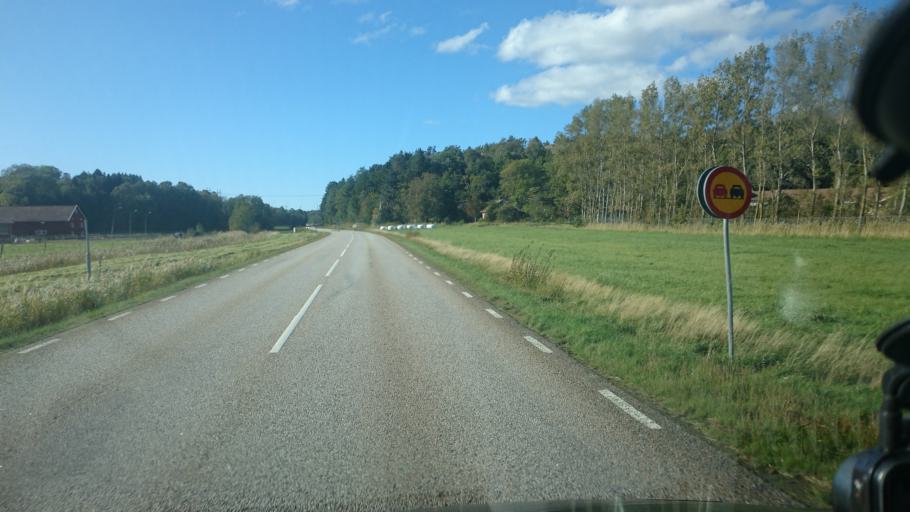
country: SE
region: Vaestra Goetaland
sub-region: Lysekils Kommun
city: Brastad
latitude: 58.3260
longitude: 11.4891
